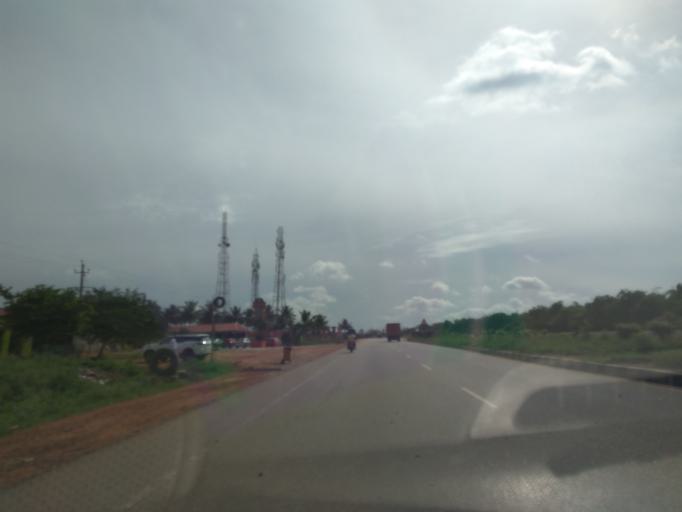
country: IN
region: Karnataka
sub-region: Bangalore Rural
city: Dasarahalli
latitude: 13.0894
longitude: 77.8343
